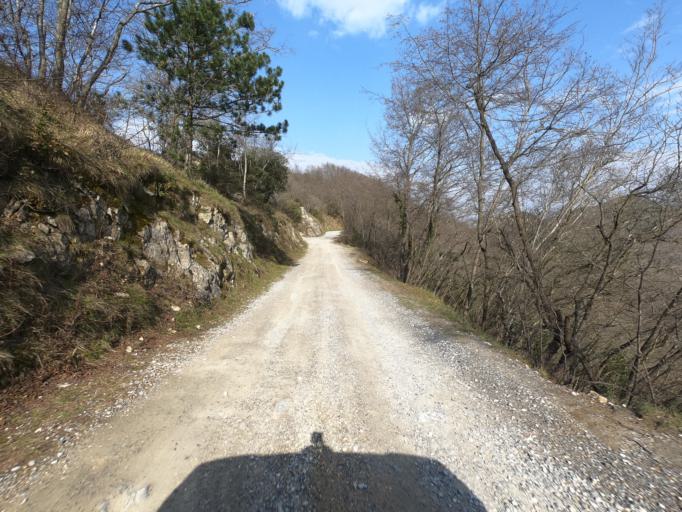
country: IT
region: Liguria
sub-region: Provincia di Savona
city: Balestrino
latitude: 44.1131
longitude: 8.1494
